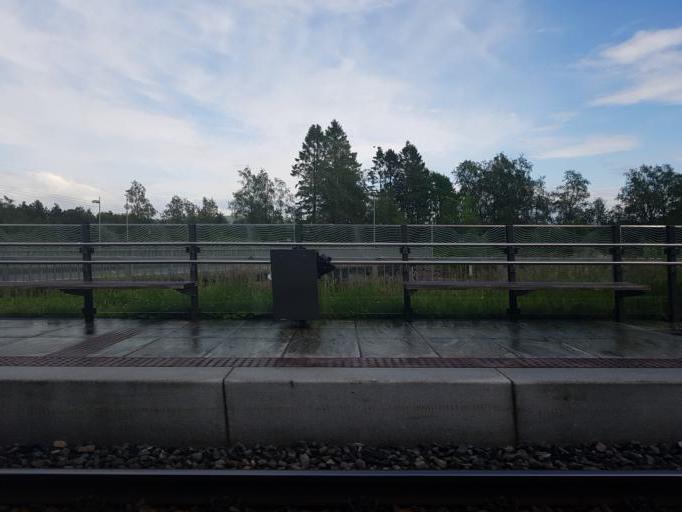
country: NO
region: Hordaland
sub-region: Bergen
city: Ytrebygda
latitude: 60.2932
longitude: 5.2674
